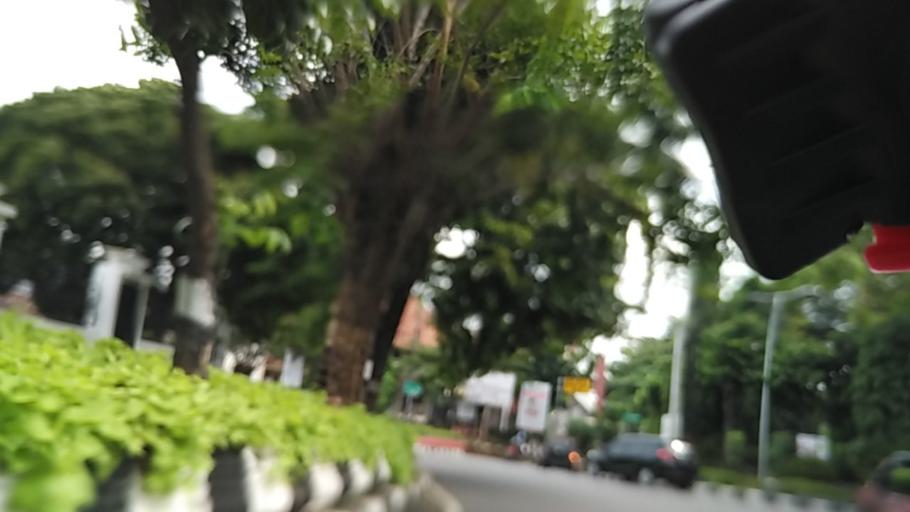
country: ID
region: Central Java
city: Semarang
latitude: -7.0071
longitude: 110.4174
